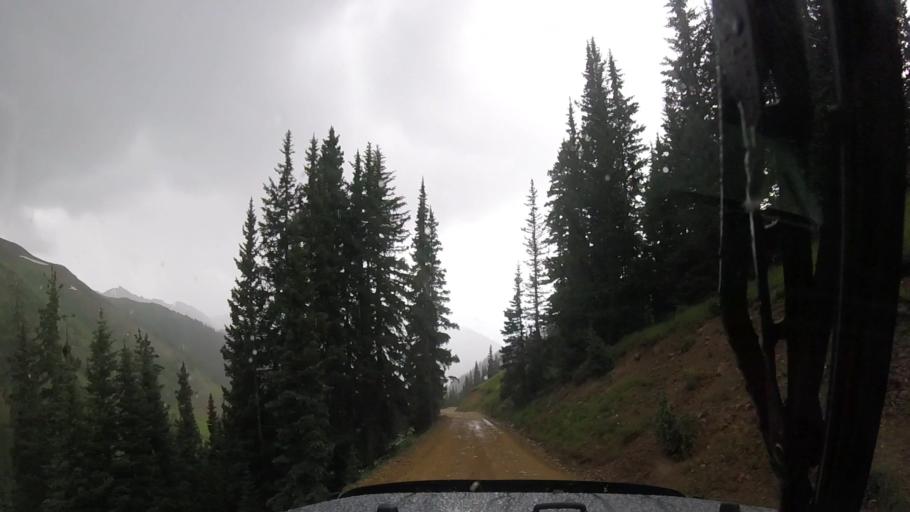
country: US
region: Colorado
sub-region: San Juan County
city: Silverton
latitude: 37.9090
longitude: -107.6450
